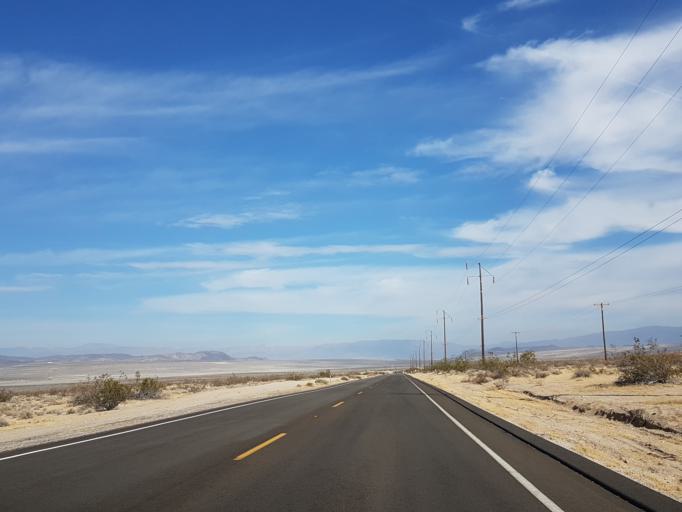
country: US
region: California
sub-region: Kern County
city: Ridgecrest
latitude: 35.6410
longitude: -117.5542
